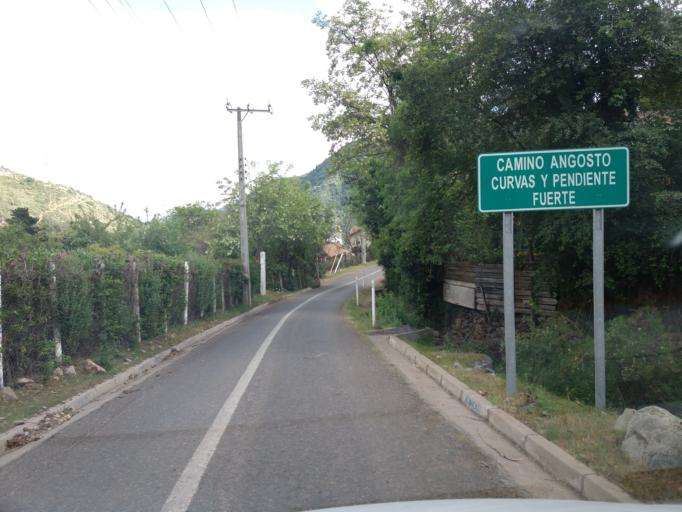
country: CL
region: Valparaiso
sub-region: Provincia de Marga Marga
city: Limache
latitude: -33.0688
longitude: -71.0633
